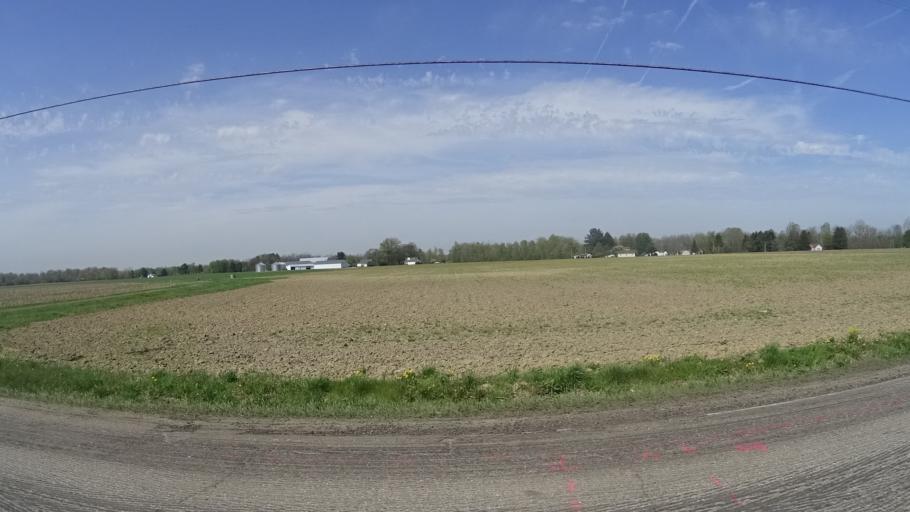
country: US
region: Ohio
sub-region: Lorain County
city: Elyria
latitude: 41.3085
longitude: -82.1177
